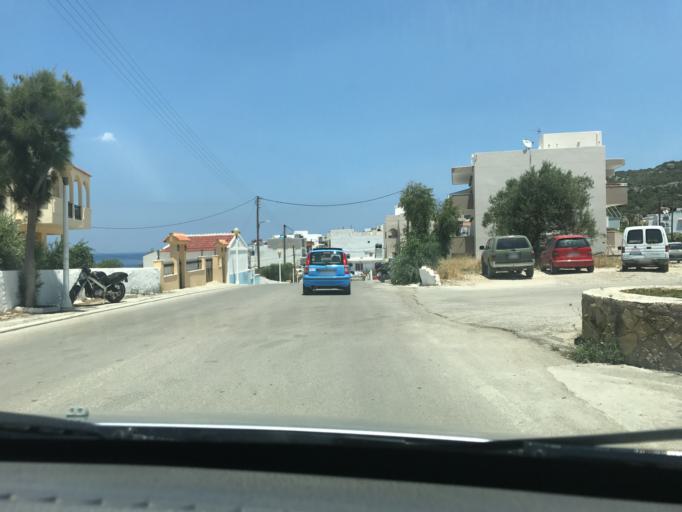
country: GR
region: South Aegean
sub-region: Nomos Dodekanisou
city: Karpathos
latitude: 35.5031
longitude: 27.2112
